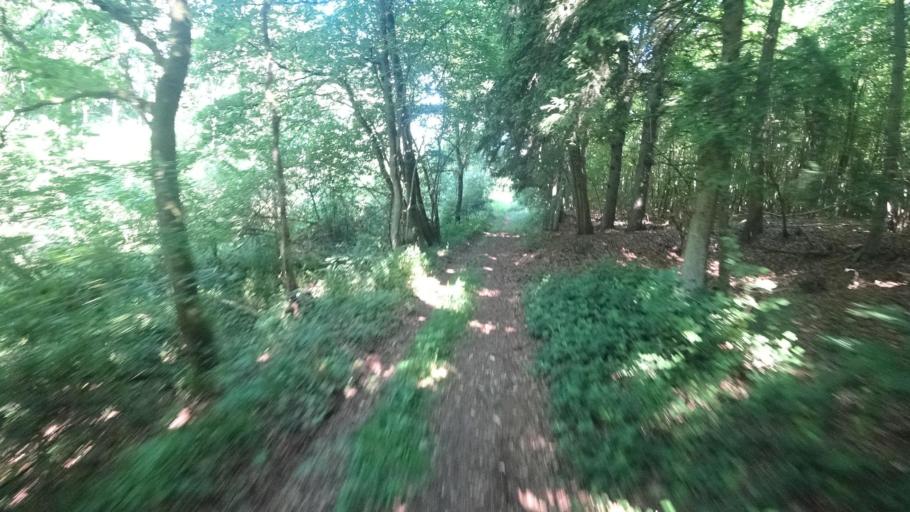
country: DE
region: Rheinland-Pfalz
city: Sorth
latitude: 50.7000
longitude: 7.6984
